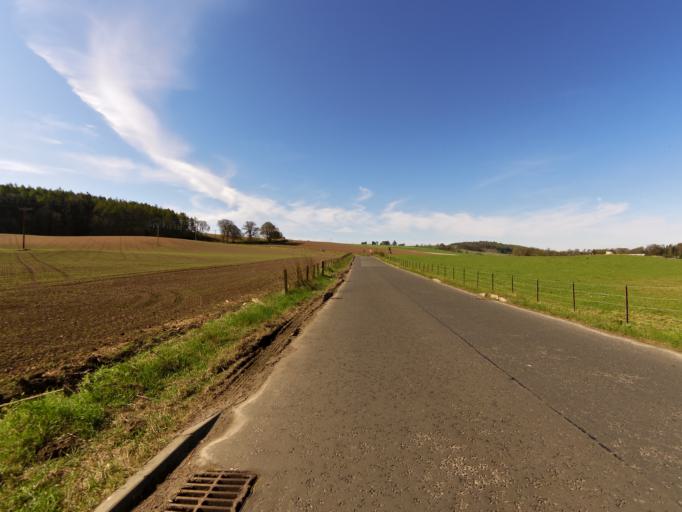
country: GB
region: Scotland
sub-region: Dundee City
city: Dundee
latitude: 56.4093
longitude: -2.9988
